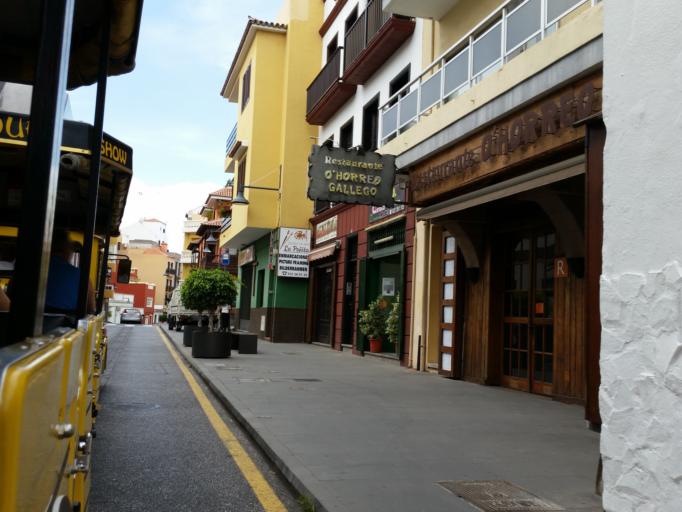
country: ES
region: Canary Islands
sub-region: Provincia de Santa Cruz de Tenerife
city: Puerto de la Cruz
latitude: 28.4166
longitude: -16.5531
